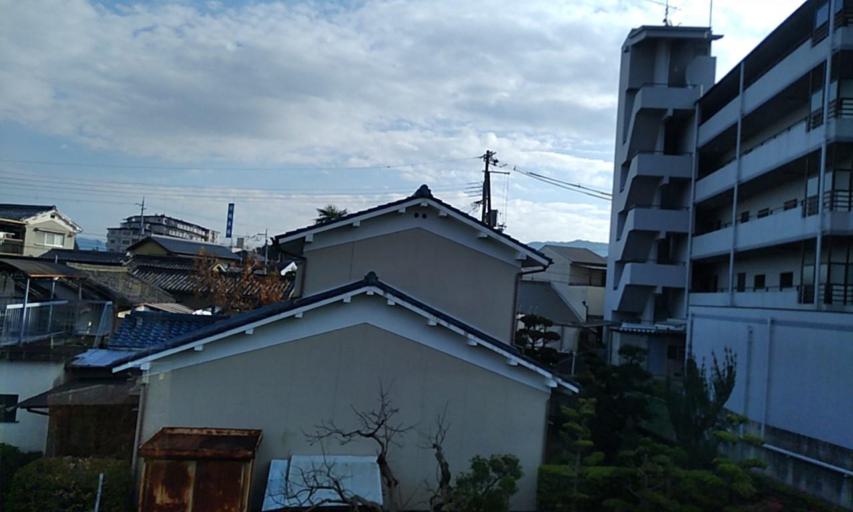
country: JP
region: Nara
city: Kashihara-shi
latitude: 34.4788
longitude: 135.7945
